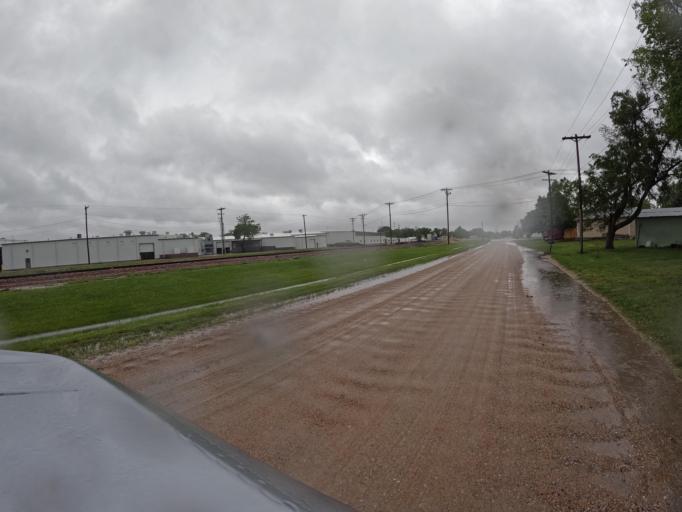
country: US
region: Nebraska
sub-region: Saline County
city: Wilber
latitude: 40.3937
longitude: -96.9161
